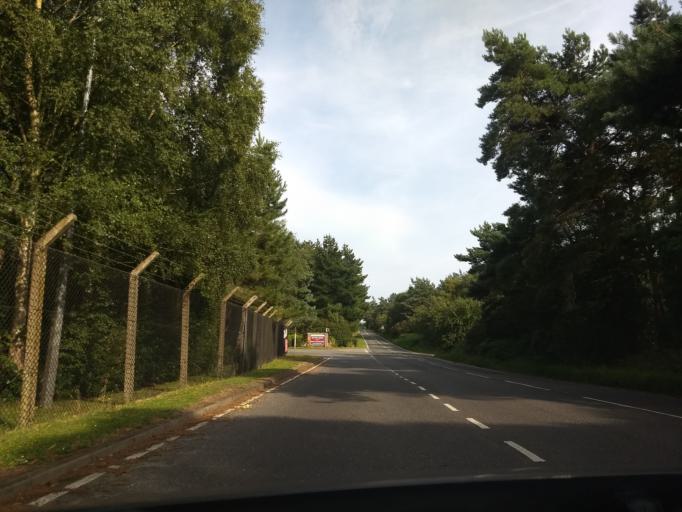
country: GB
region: England
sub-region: Suffolk
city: Woodbridge
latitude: 52.0801
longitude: 1.3852
